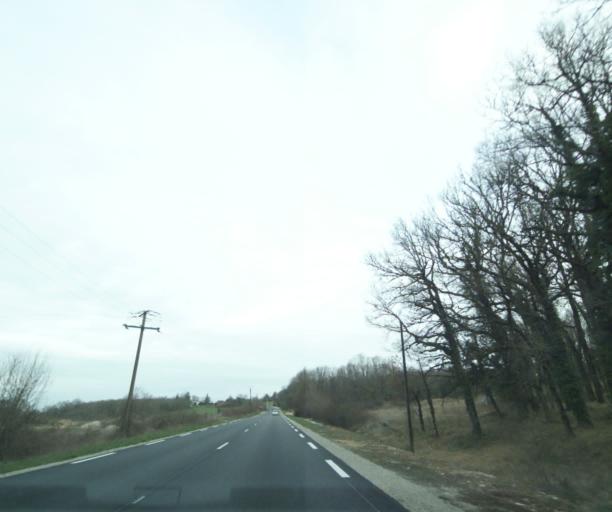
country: FR
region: Limousin
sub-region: Departement de la Correze
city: Brive-la-Gaillarde
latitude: 45.0297
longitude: 1.5120
